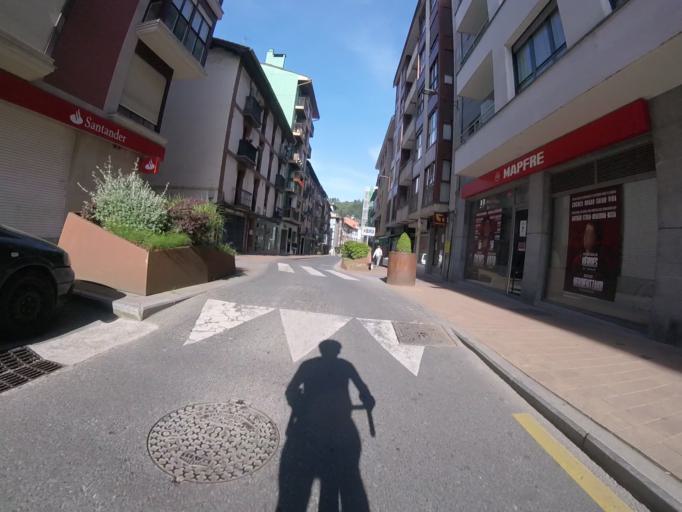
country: ES
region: Basque Country
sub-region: Provincia de Guipuzcoa
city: Villafranca de Ordizia
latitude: 43.0535
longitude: -2.1815
